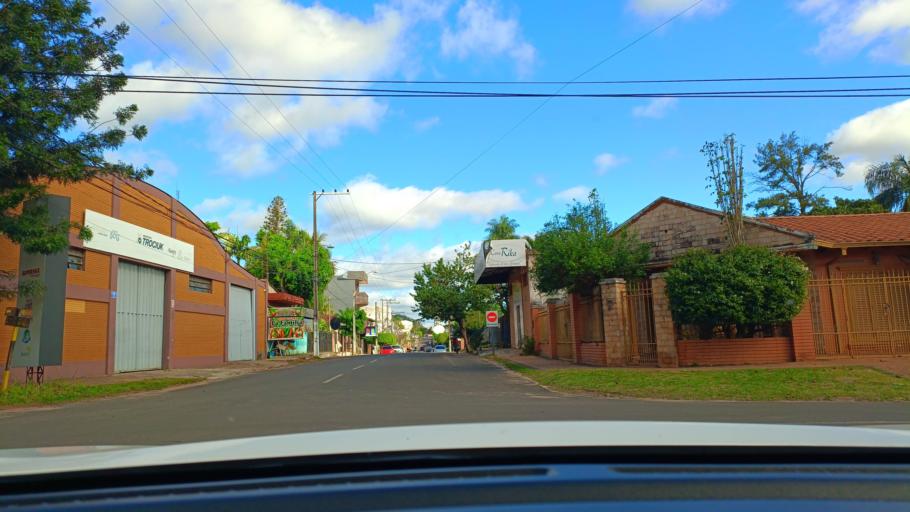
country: PY
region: San Pedro
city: Guayaybi
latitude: -24.6609
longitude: -56.4440
